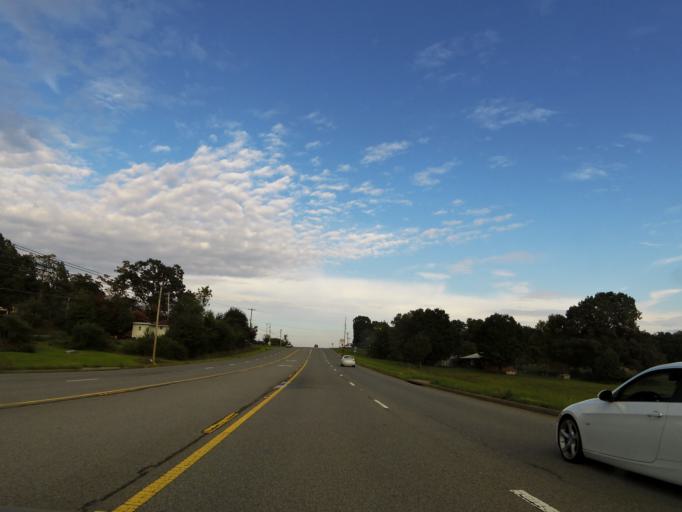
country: US
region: Alabama
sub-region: Lauderdale County
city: Rogersville
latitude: 34.8159
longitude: -87.2626
